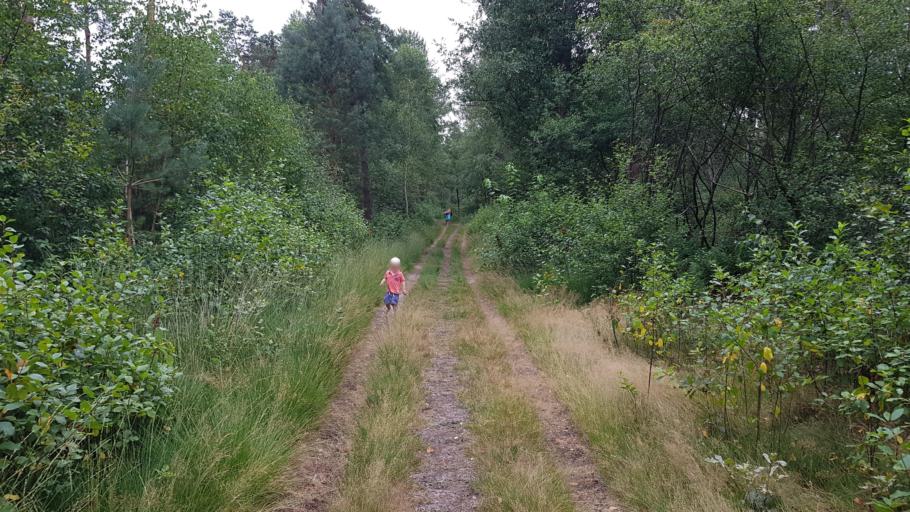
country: NL
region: Utrecht
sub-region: Gemeente Utrechtse Heuvelrug
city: Maarsbergen
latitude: 52.0440
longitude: 5.4257
